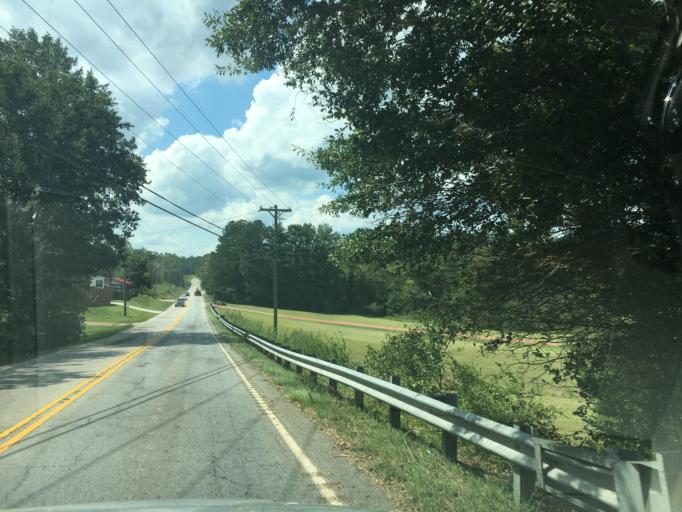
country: US
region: South Carolina
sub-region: Greenville County
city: Berea
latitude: 34.8914
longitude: -82.4927
